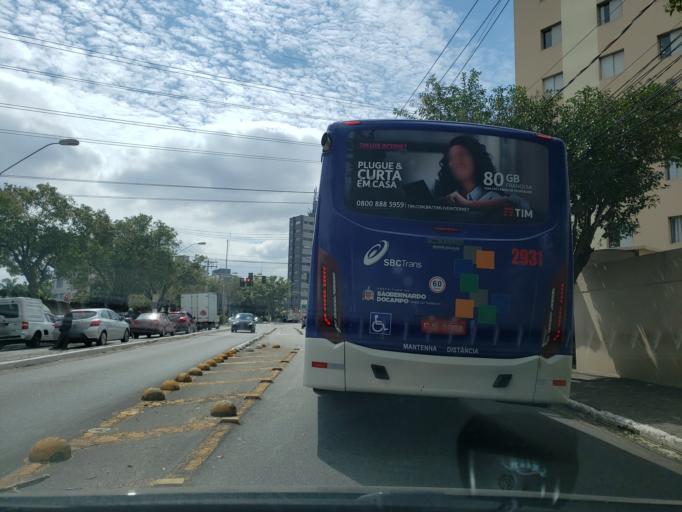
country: BR
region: Sao Paulo
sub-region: Sao Bernardo Do Campo
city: Sao Bernardo do Campo
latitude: -23.6722
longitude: -46.5683
